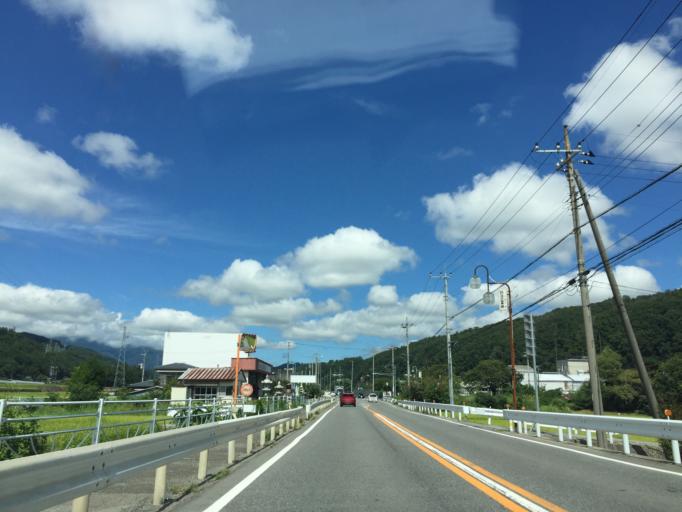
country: JP
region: Yamanashi
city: Nirasaki
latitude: 35.7900
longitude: 138.3768
